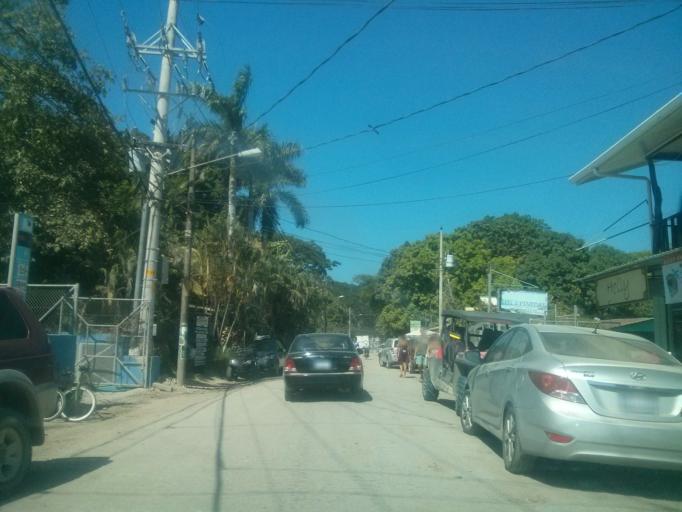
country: CR
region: Guanacaste
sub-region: Canton de Nandayure
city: Bejuco
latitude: 9.6283
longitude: -85.1508
